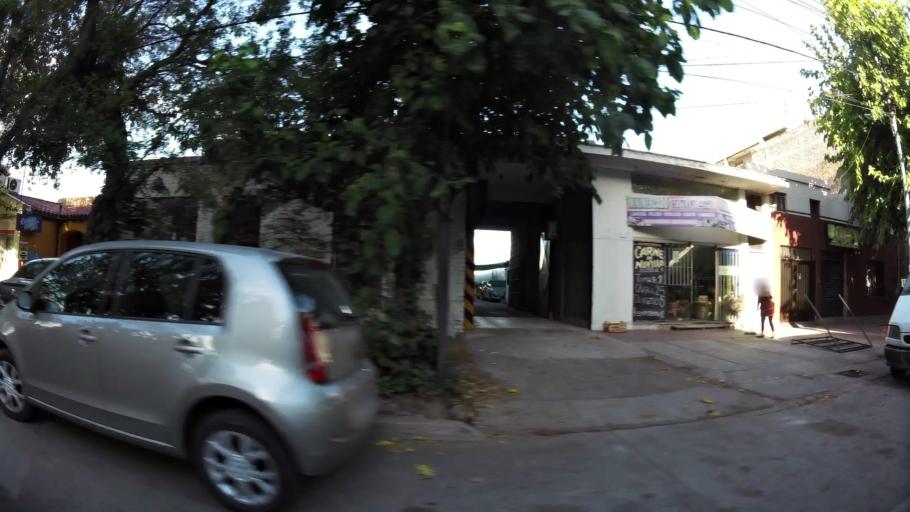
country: AR
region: Mendoza
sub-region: Departamento de Godoy Cruz
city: Godoy Cruz
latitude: -32.9070
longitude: -68.8516
